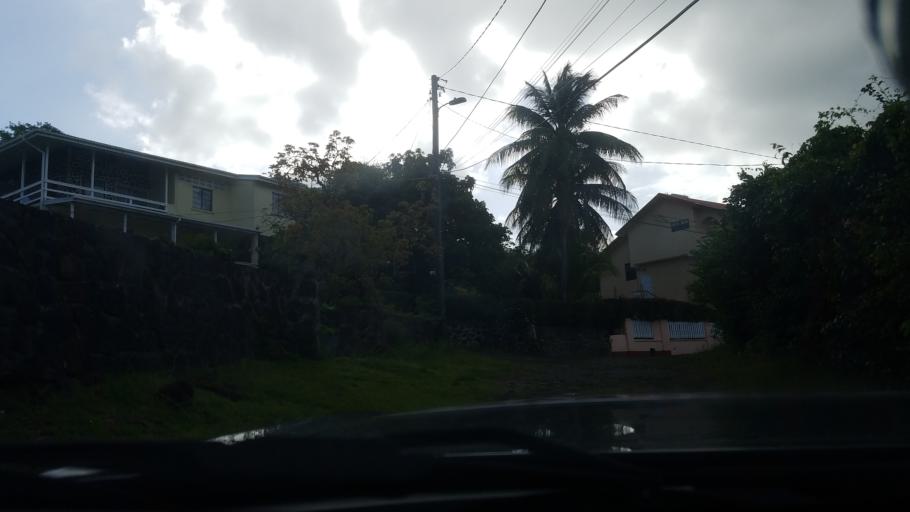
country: LC
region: Gros-Islet
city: Gros Islet
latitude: 14.0615
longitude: -60.9595
